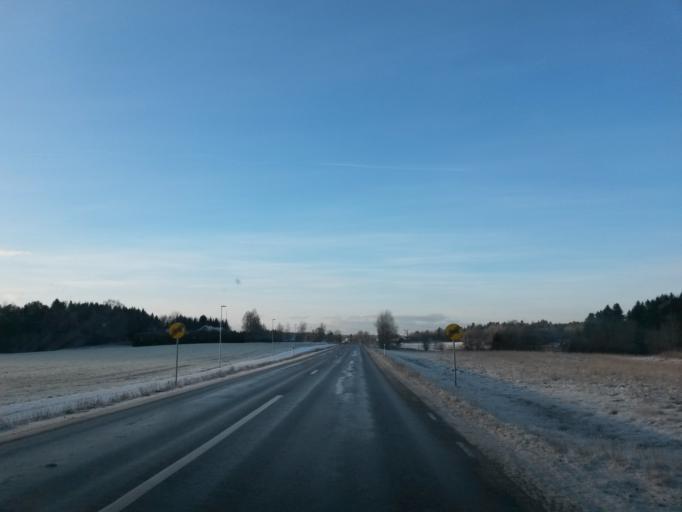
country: SE
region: Vaestra Goetaland
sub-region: Alingsas Kommun
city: Sollebrunn
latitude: 58.1082
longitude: 12.5937
